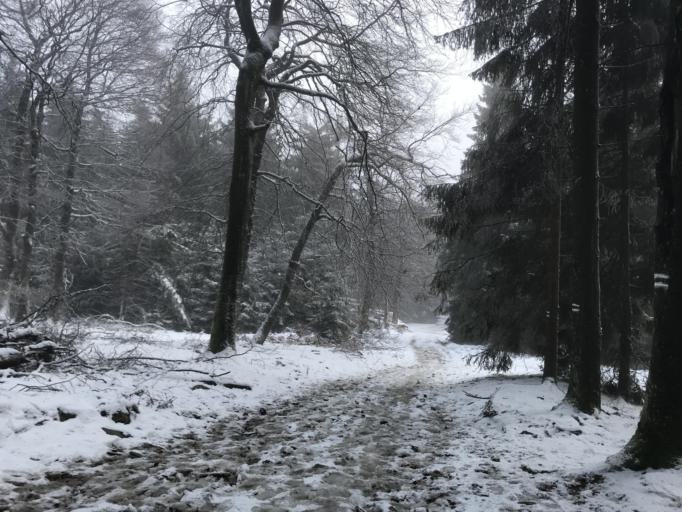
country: DE
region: Hesse
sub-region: Regierungsbezirk Darmstadt
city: Konigstein im Taunus
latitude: 50.2185
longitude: 8.4596
